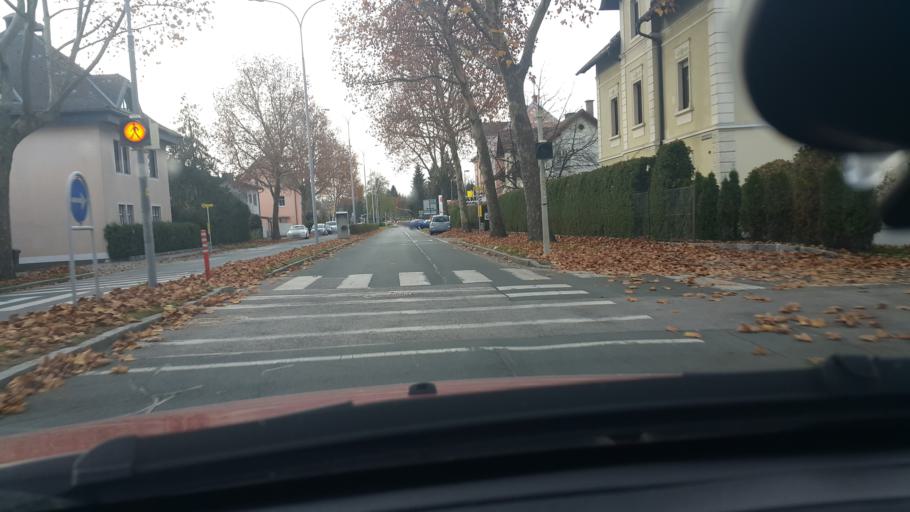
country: AT
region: Carinthia
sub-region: Klagenfurt am Woerthersee
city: Klagenfurt am Woerthersee
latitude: 46.6235
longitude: 14.2865
